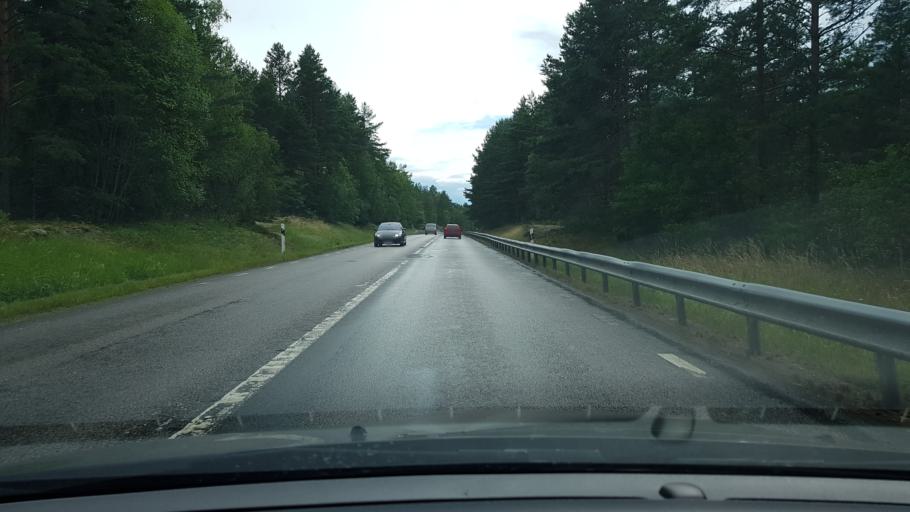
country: SE
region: Uppsala
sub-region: Uppsala Kommun
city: Saevja
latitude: 59.7994
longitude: 17.6821
